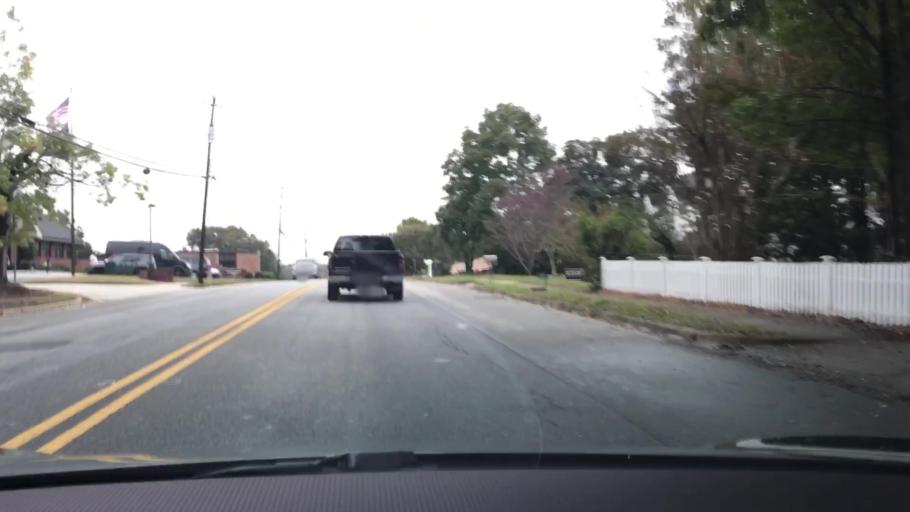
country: US
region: Georgia
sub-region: Greene County
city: Greensboro
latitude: 33.5694
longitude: -83.1834
